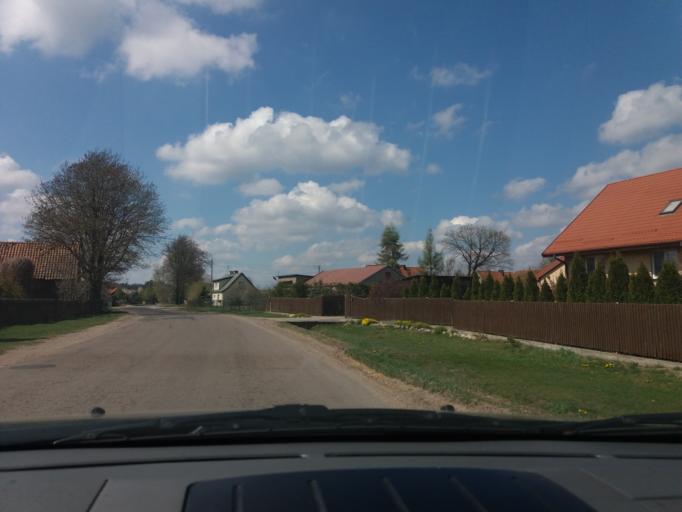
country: PL
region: Warmian-Masurian Voivodeship
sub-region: Powiat szczycienski
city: Jedwabno
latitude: 53.3625
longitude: 20.6418
